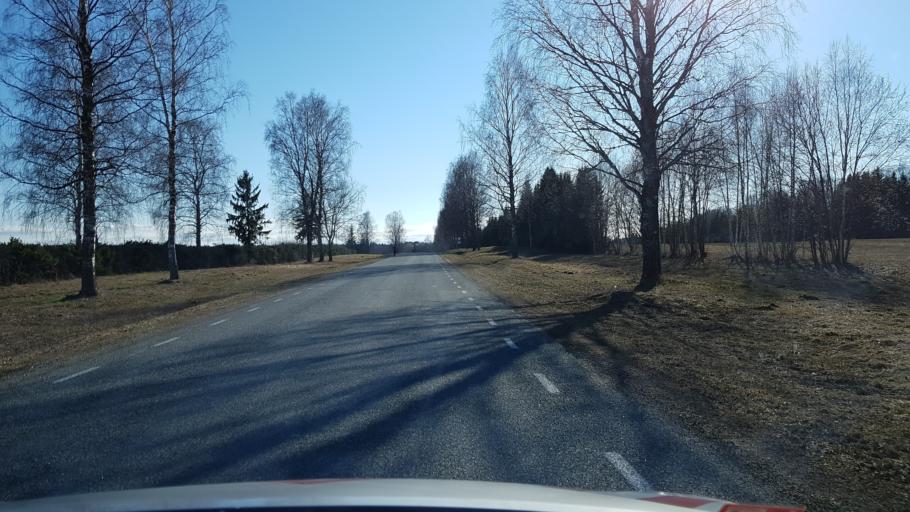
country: EE
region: Laeaene-Virumaa
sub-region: Kadrina vald
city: Kadrina
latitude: 59.3338
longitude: 26.1122
